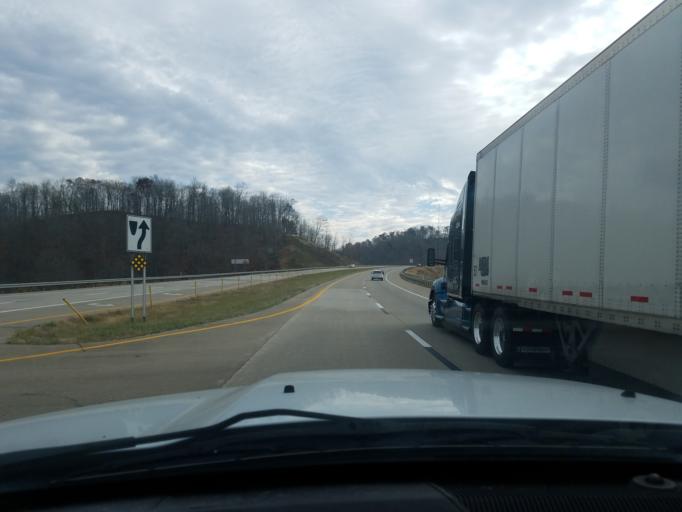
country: US
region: West Virginia
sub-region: Putnam County
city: Eleanor
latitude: 38.5232
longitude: -81.9347
